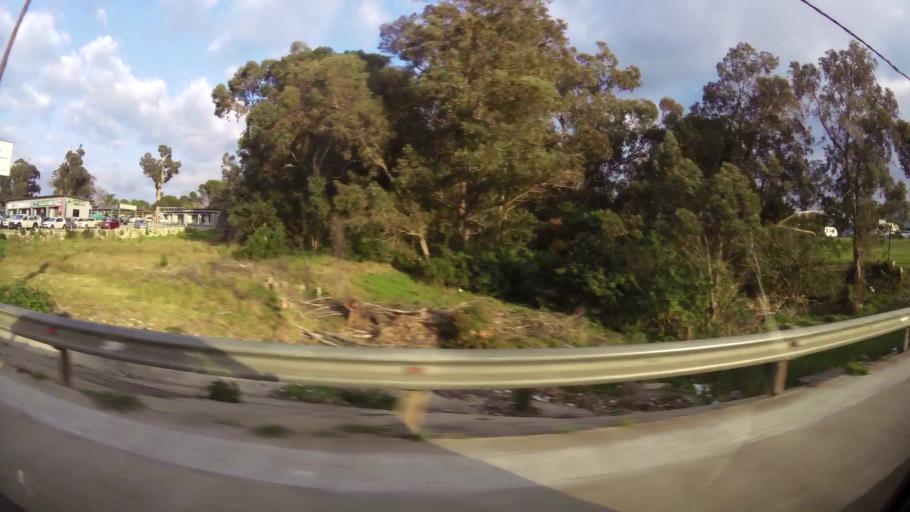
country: ZA
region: Eastern Cape
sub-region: Nelson Mandela Bay Metropolitan Municipality
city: Port Elizabeth
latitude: -33.9758
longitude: 25.5539
